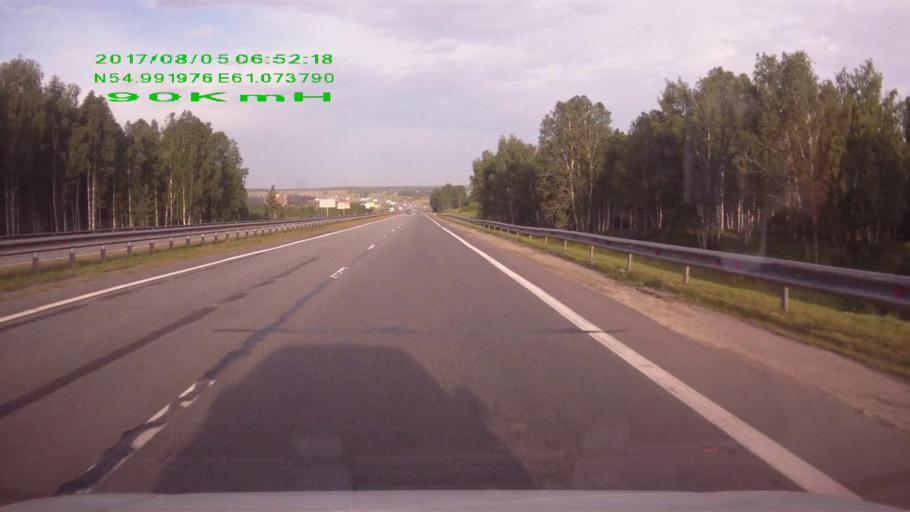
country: RU
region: Chelyabinsk
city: Poletayevo
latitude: 54.9919
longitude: 61.0727
